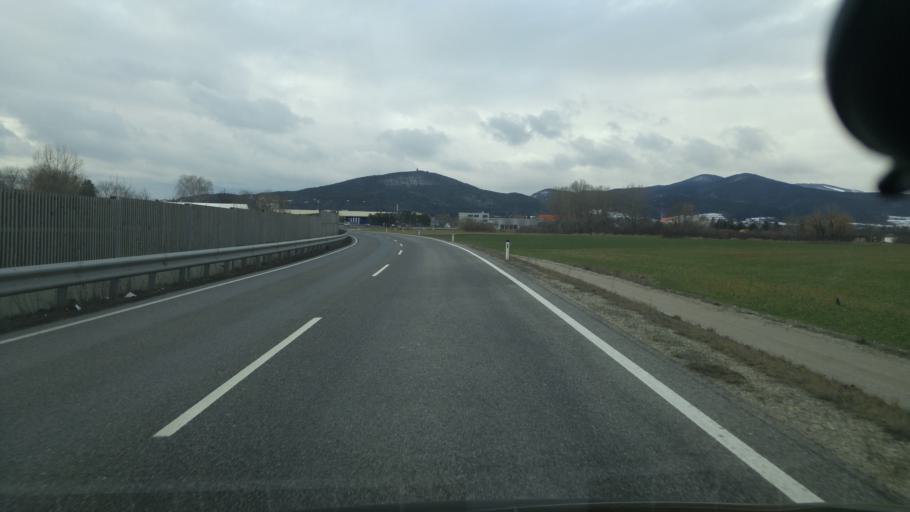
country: AT
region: Lower Austria
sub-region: Politischer Bezirk Baden
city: Bad Voslau
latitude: 47.9752
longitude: 16.2331
